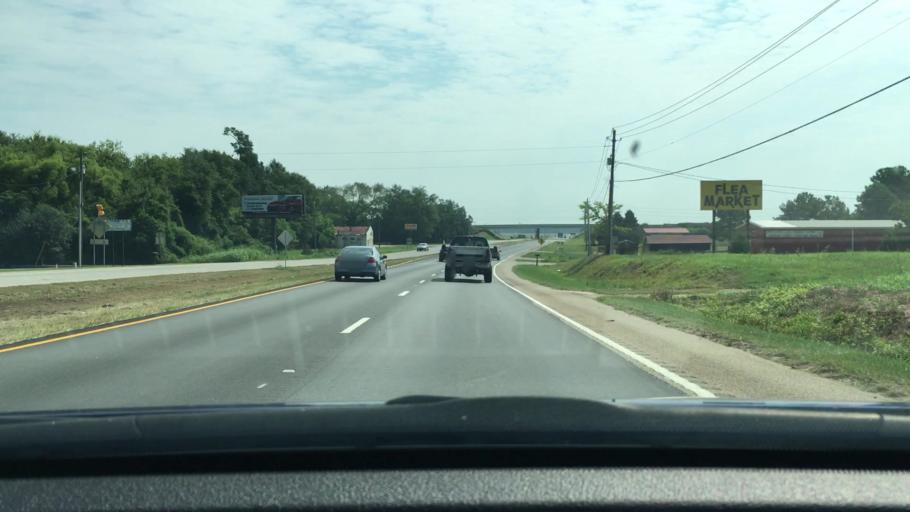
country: US
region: South Carolina
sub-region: Sumter County
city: Oakland
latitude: 33.9524
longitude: -80.4952
